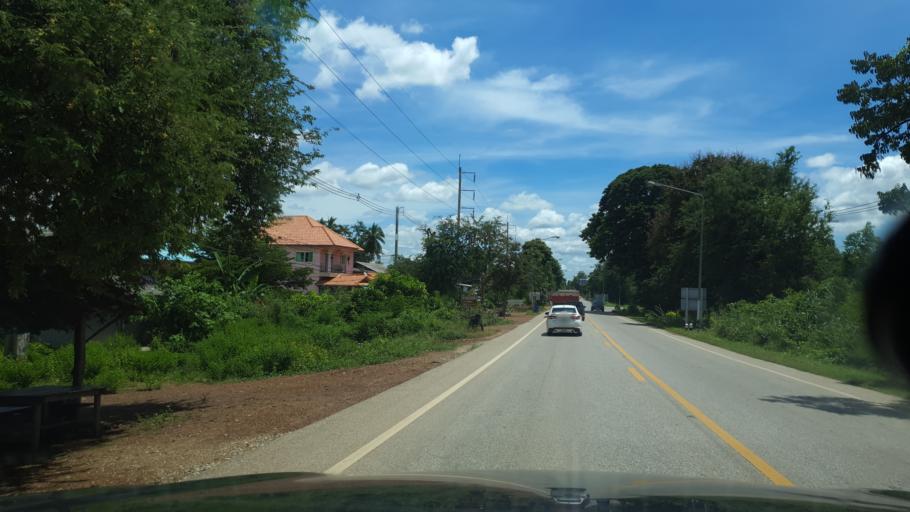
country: TH
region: Sukhothai
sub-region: Amphoe Si Satchanalai
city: Si Satchanalai
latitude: 17.4372
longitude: 99.8009
